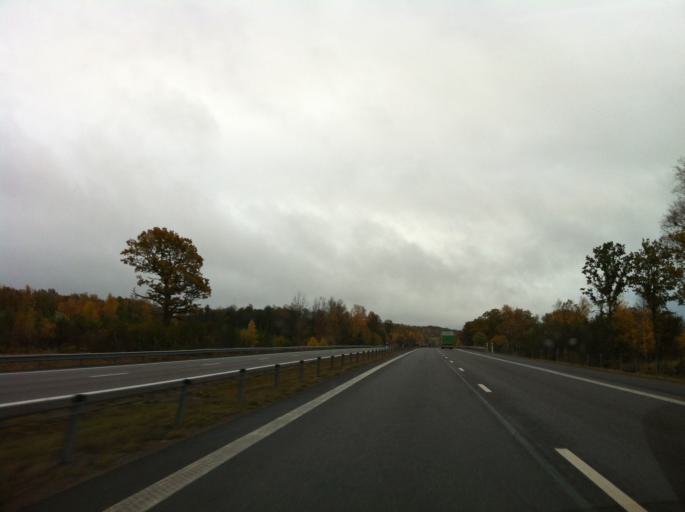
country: SE
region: Joenkoeping
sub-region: Jonkopings Kommun
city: Graenna
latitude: 58.0410
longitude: 14.4982
